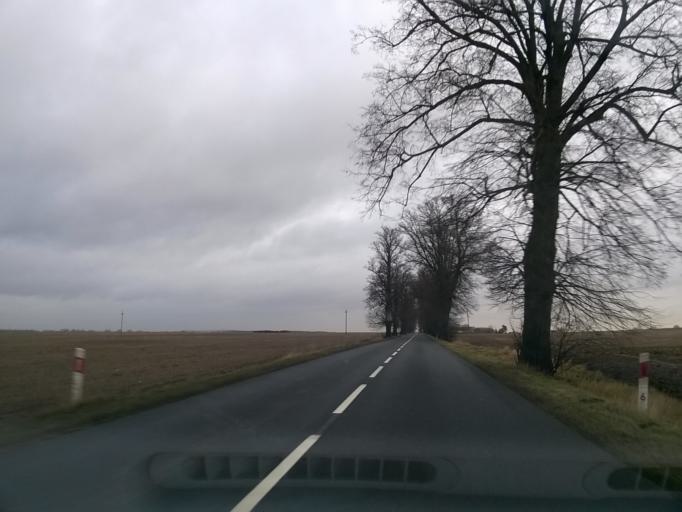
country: PL
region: Greater Poland Voivodeship
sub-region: Powiat wagrowiecki
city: Wapno
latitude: 52.9525
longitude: 17.4168
